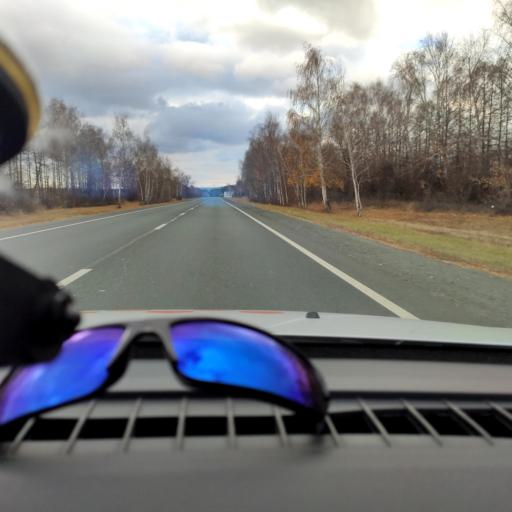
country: RU
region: Samara
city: Volzhskiy
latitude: 53.4618
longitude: 50.1274
